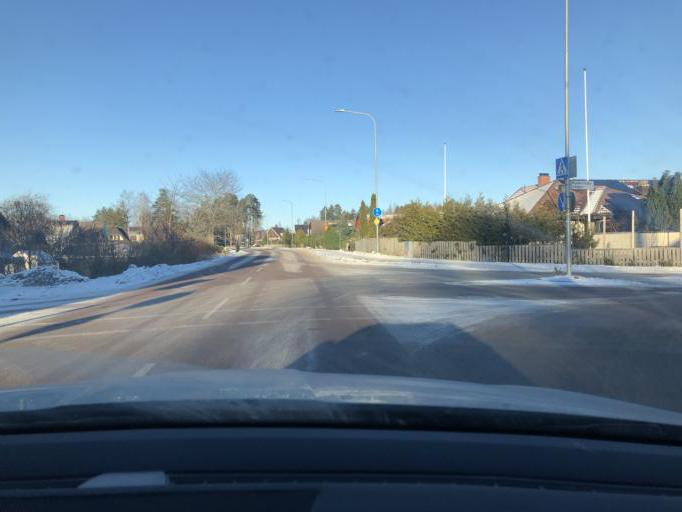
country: SE
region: Vaestmanland
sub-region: Vasteras
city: Hokasen
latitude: 59.6641
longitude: 16.5921
